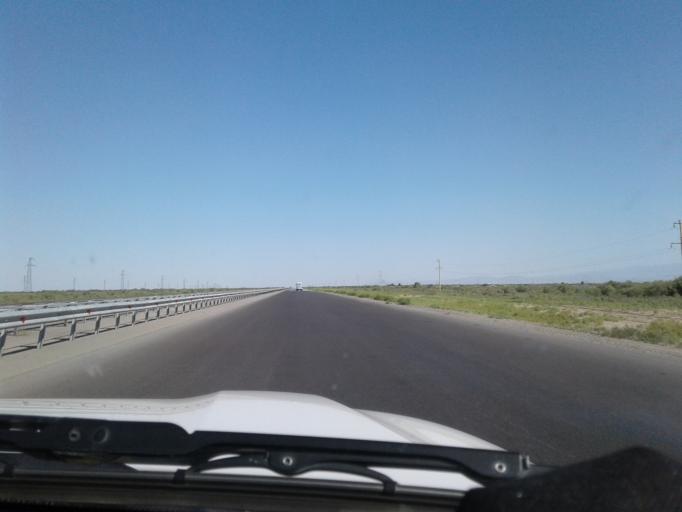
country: TM
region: Ahal
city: Kaka
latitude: 37.5049
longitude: 59.4493
